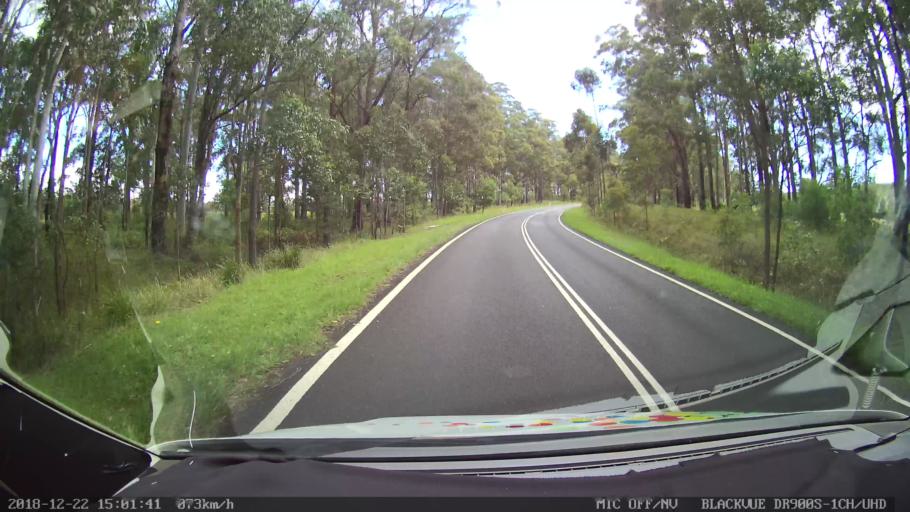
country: AU
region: New South Wales
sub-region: Bellingen
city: Dorrigo
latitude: -30.2571
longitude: 152.4575
